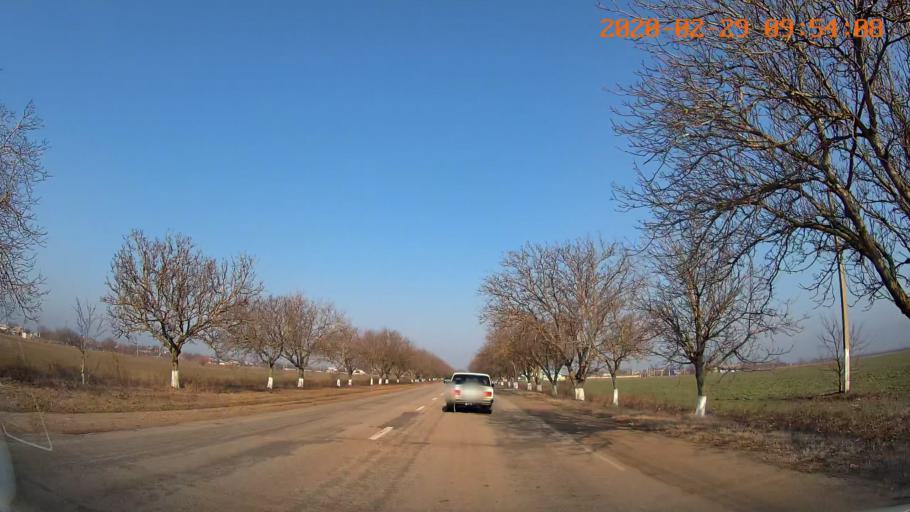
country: MD
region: Telenesti
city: Slobozia
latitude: 46.7265
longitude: 29.7177
